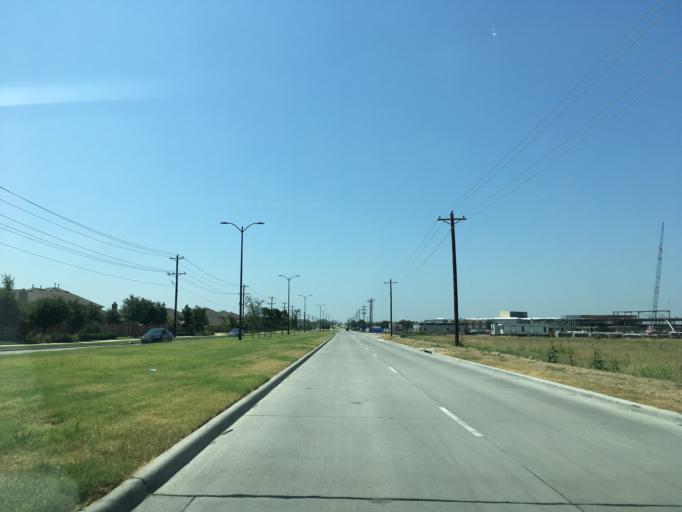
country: US
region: Texas
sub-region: Collin County
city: Prosper
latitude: 33.2136
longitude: -96.7677
